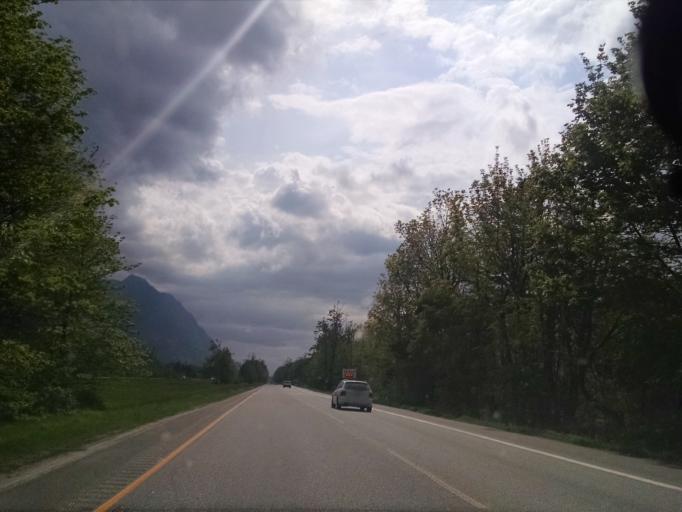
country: CA
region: British Columbia
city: Hope
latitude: 49.3508
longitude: -121.5853
